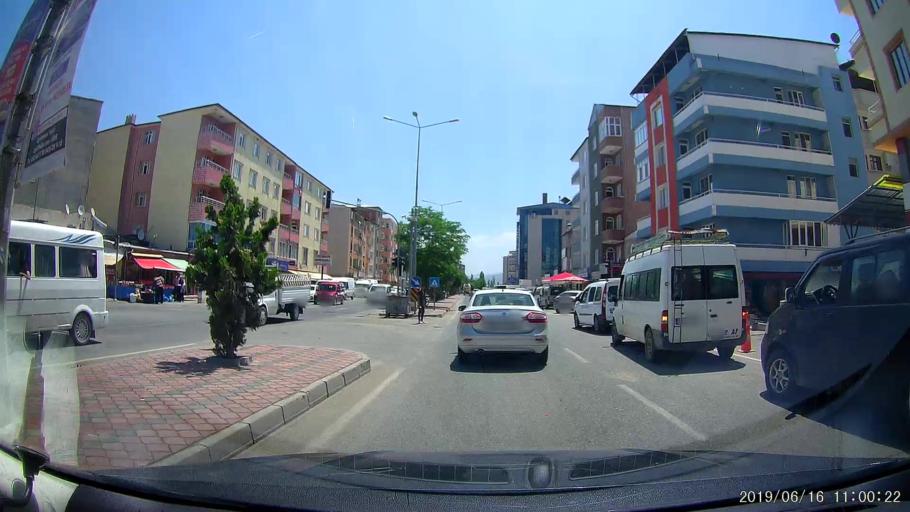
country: TR
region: Igdir
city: Igdir
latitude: 39.9186
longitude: 44.0433
